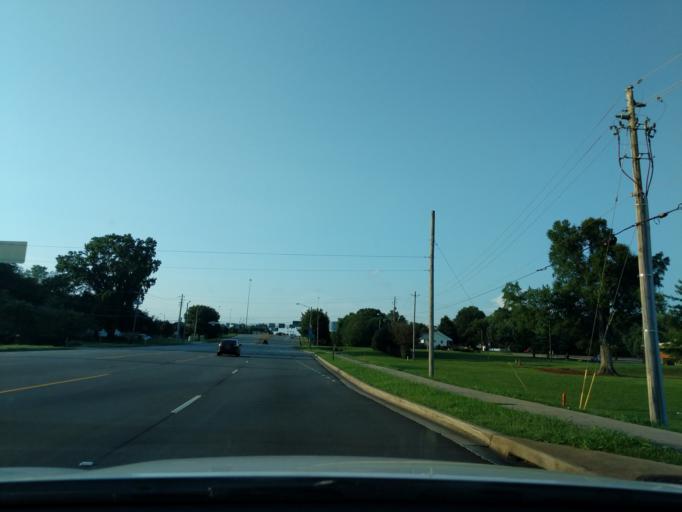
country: US
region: Alabama
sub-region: Madison County
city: Redstone Arsenal
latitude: 34.7145
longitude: -86.6270
